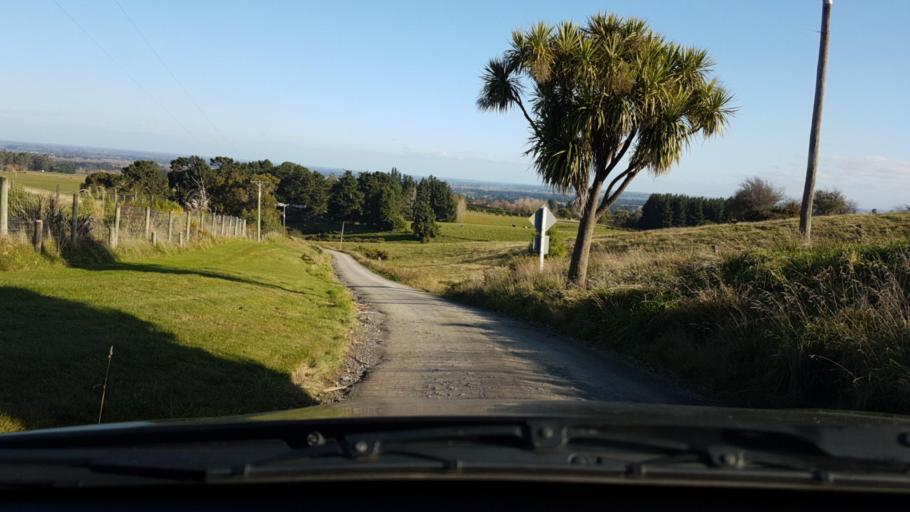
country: NZ
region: Canterbury
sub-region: Waimakariri District
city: Woodend
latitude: -43.2452
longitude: 172.5767
